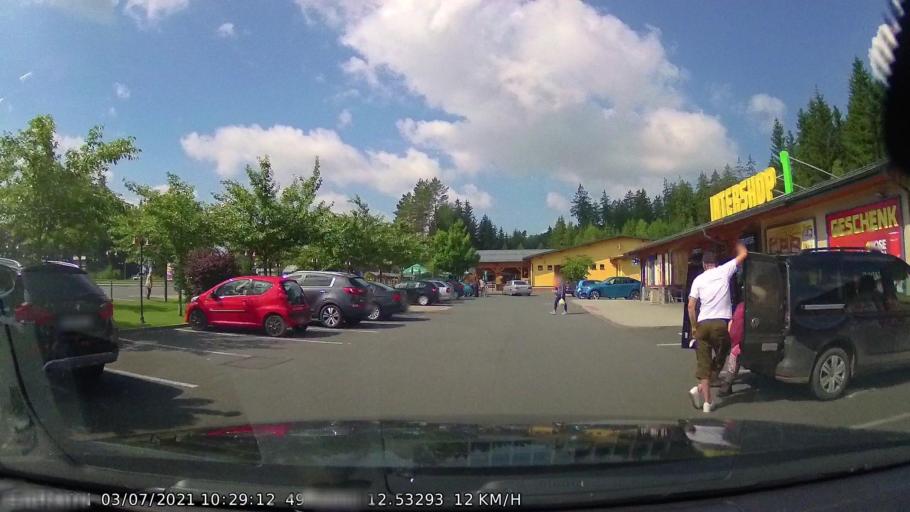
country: DE
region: Bavaria
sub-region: Upper Palatinate
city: Waidhaus
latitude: 49.6596
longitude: 12.5329
